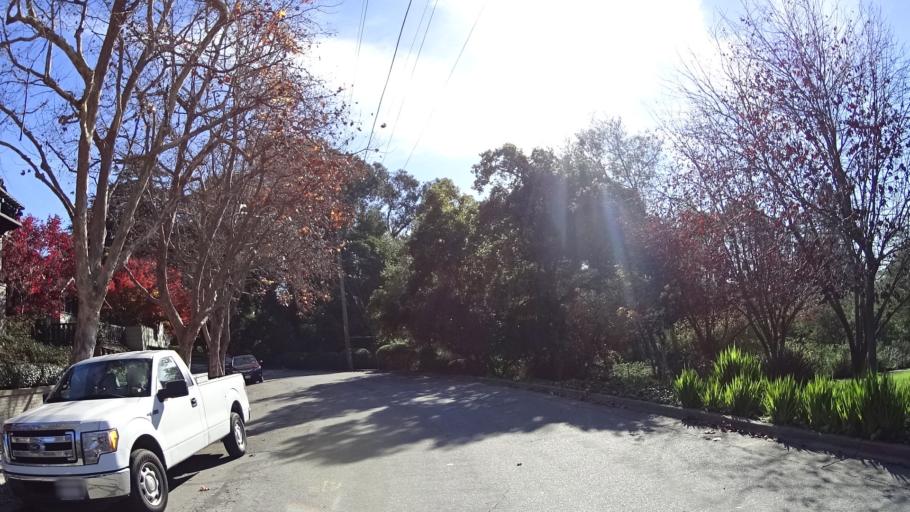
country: US
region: California
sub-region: Alameda County
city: Piedmont
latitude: 37.8272
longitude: -122.2380
